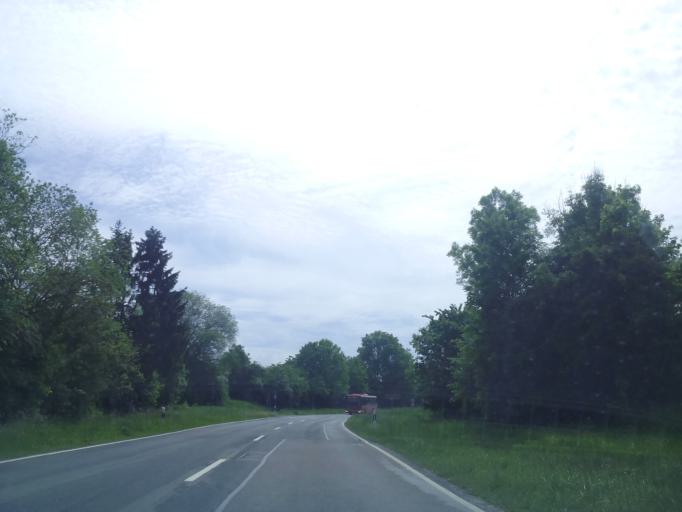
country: DE
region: Bavaria
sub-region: Upper Franconia
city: Coburg
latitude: 50.2620
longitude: 10.9352
